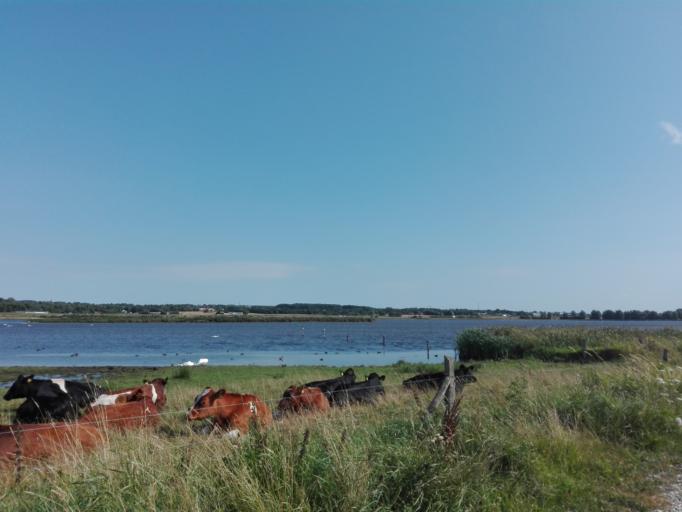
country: DK
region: Central Jutland
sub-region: Arhus Kommune
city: Lystrup
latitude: 56.2143
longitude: 10.2174
